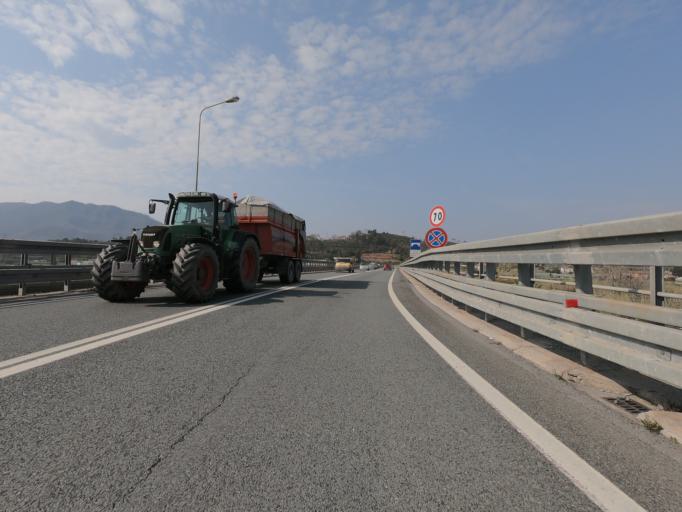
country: IT
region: Liguria
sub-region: Provincia di Savona
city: San Fedele-Lusignano
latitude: 44.0681
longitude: 8.1695
